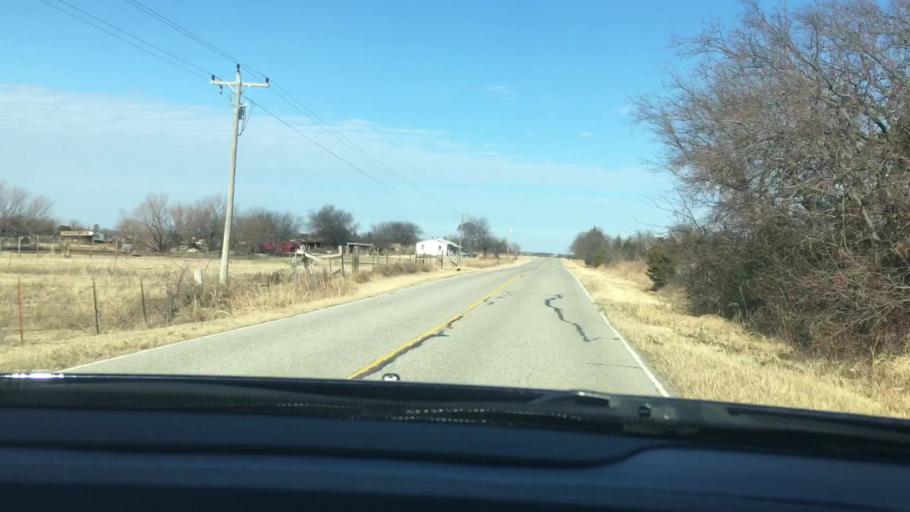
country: US
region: Oklahoma
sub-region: Garvin County
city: Wynnewood
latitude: 34.7038
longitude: -97.1254
